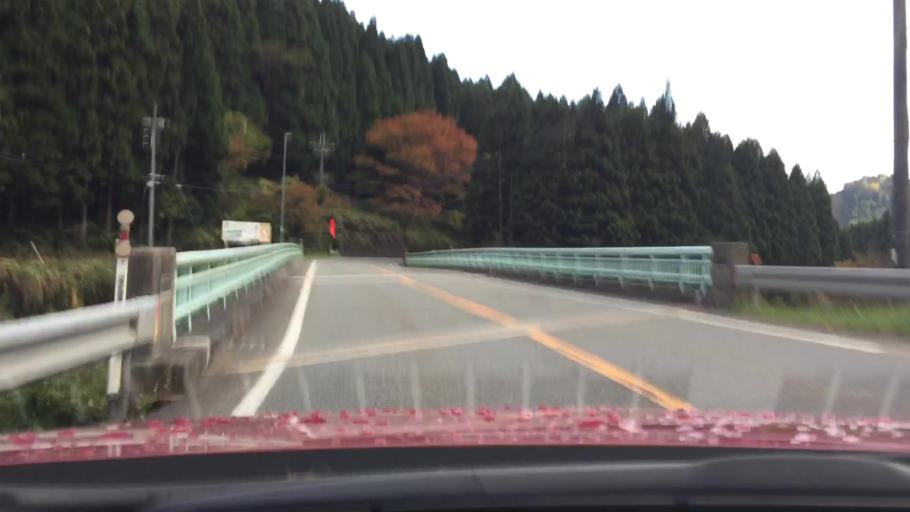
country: JP
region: Hyogo
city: Yamazakicho-nakabirose
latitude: 35.1822
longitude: 134.5347
